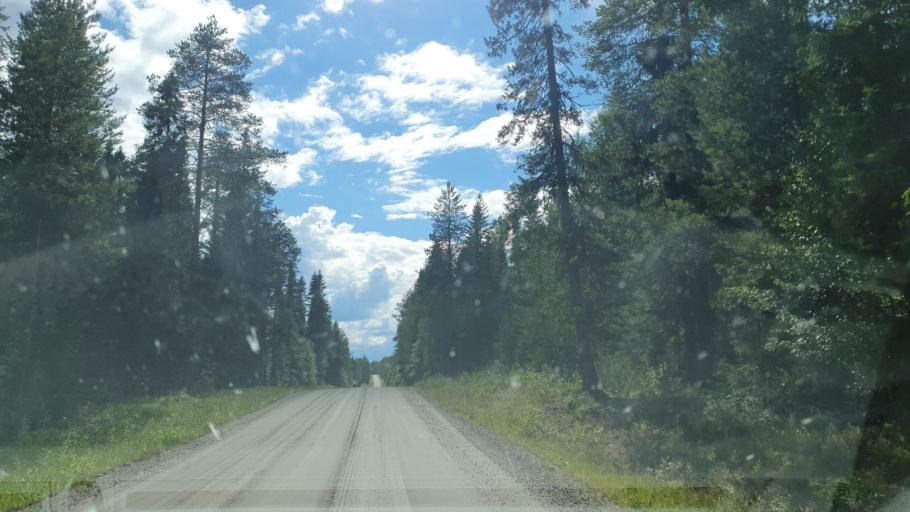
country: FI
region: Kainuu
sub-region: Kehys-Kainuu
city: Kuhmo
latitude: 64.1483
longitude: 29.7205
